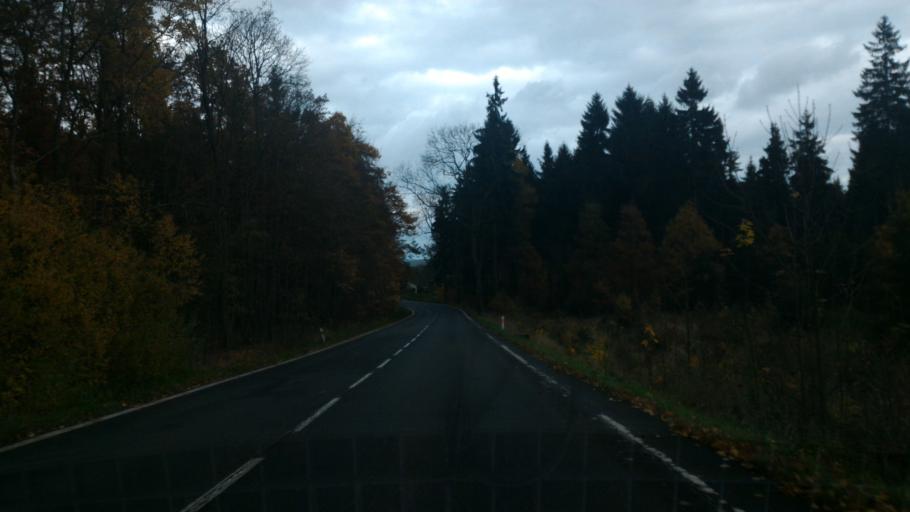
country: CZ
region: Ustecky
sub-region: Okres Decin
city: Rumburk
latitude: 50.9707
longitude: 14.5647
